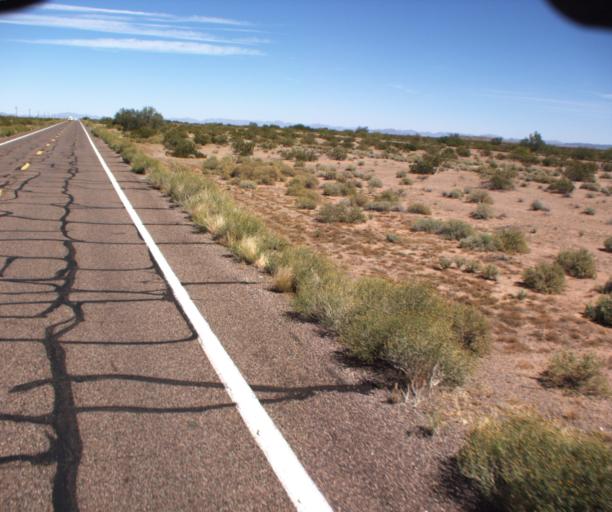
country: US
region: Arizona
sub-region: Maricopa County
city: Gila Bend
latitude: 32.7605
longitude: -112.8216
